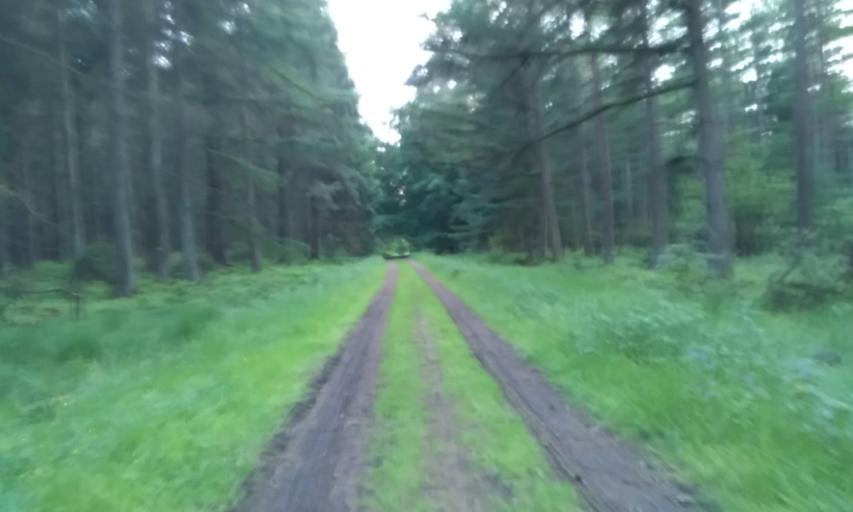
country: DE
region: Lower Saxony
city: Dollern
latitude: 53.5229
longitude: 9.5231
